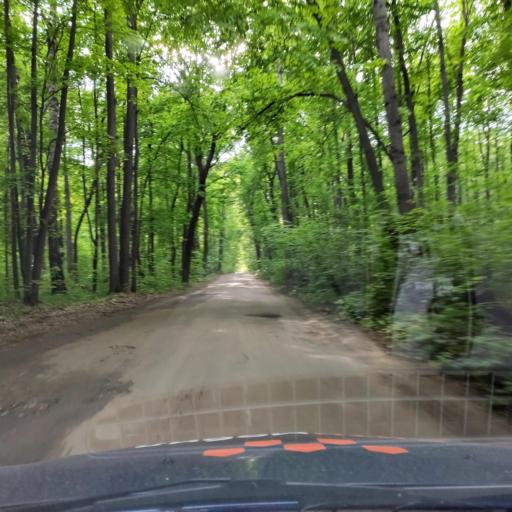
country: RU
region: Voronezj
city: Podgornoye
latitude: 51.7437
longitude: 39.2141
